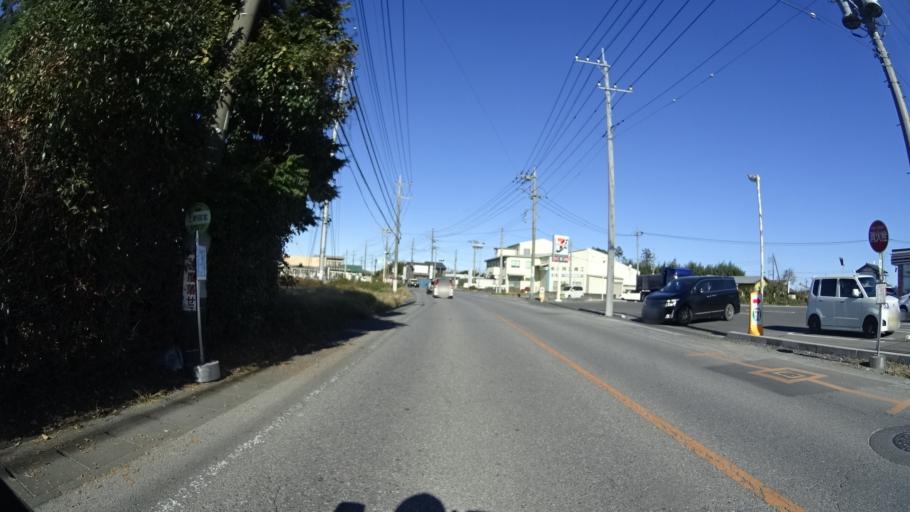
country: JP
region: Tochigi
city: Mibu
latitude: 36.4476
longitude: 139.7561
